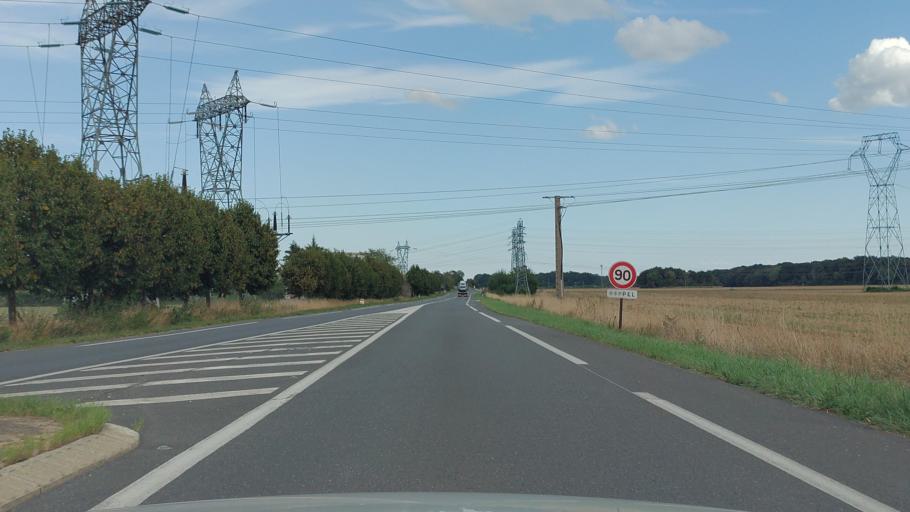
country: FR
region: Ile-de-France
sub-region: Departement de Seine-et-Marne
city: Moisenay
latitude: 48.5473
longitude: 2.7666
